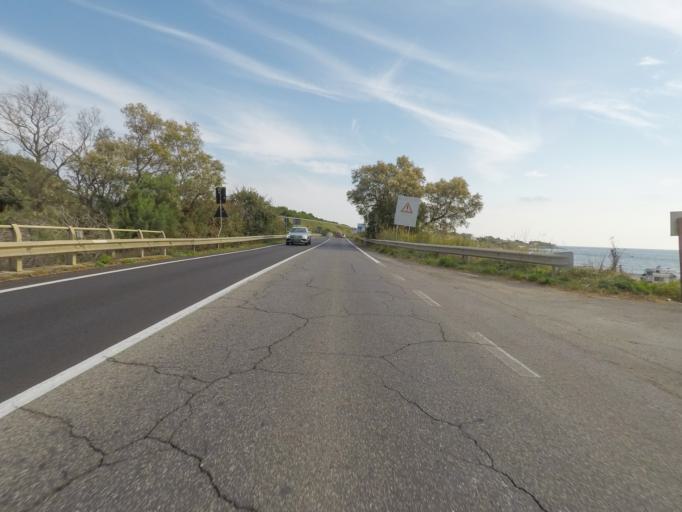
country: IT
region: Latium
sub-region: Citta metropolitana di Roma Capitale
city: Civitavecchia
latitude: 42.0580
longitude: 11.8184
